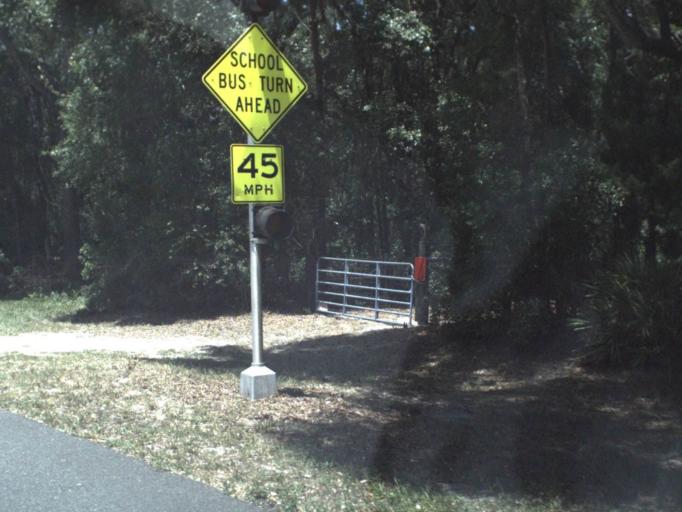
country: US
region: Florida
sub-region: Dixie County
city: Cross City
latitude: 29.7045
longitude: -82.9844
